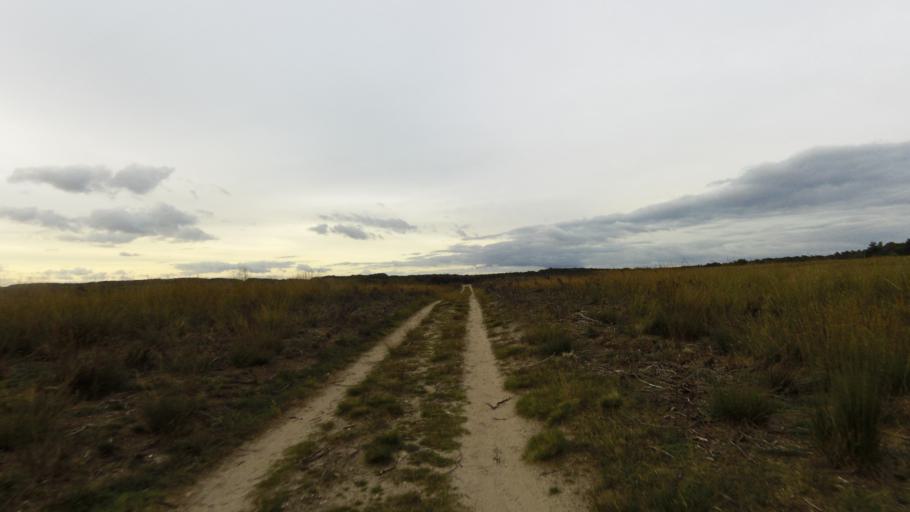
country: NL
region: Gelderland
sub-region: Gemeente Ede
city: Otterlo
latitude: 52.1666
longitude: 5.8560
